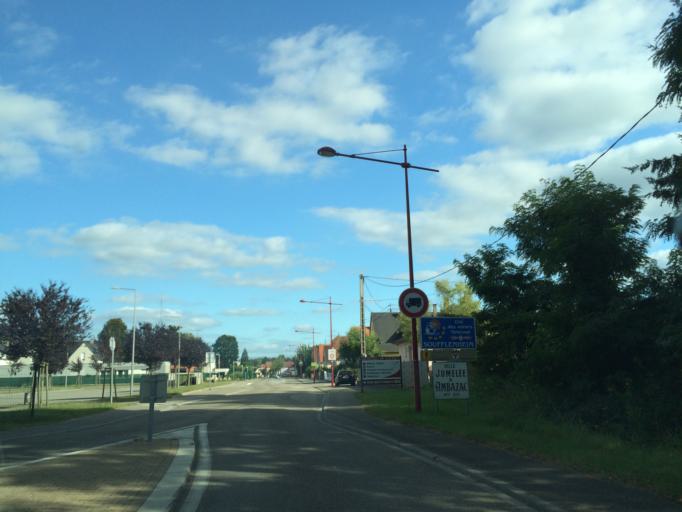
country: FR
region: Alsace
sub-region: Departement du Bas-Rhin
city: Soufflenheim
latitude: 48.8371
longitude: 7.9596
